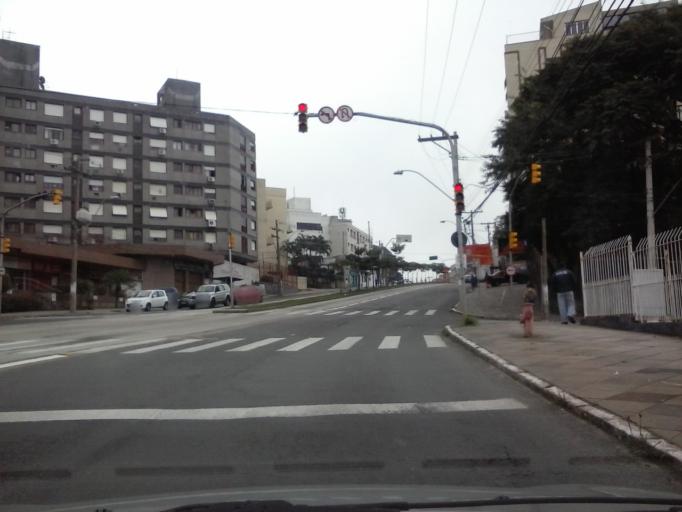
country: BR
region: Rio Grande do Sul
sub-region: Porto Alegre
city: Porto Alegre
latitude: -30.0410
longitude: -51.1702
